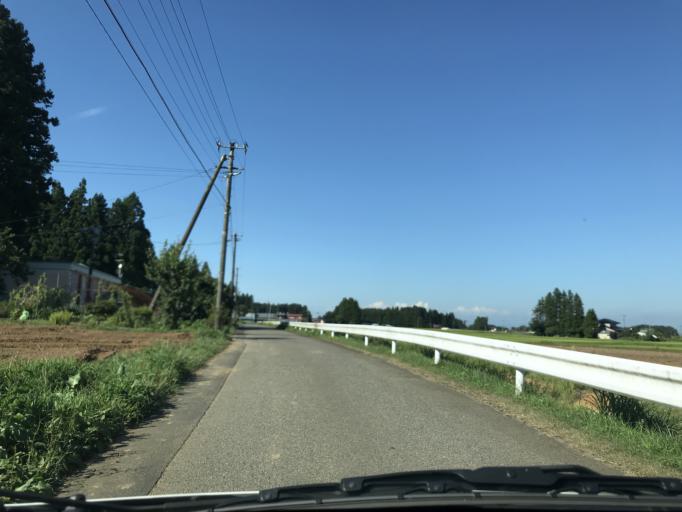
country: JP
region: Iwate
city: Mizusawa
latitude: 39.0725
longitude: 141.0471
